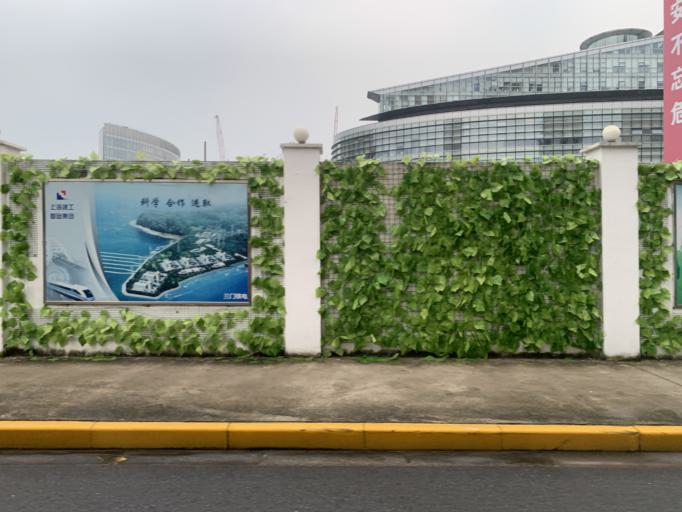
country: CN
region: Shanghai Shi
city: Huamu
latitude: 31.2237
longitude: 121.5469
